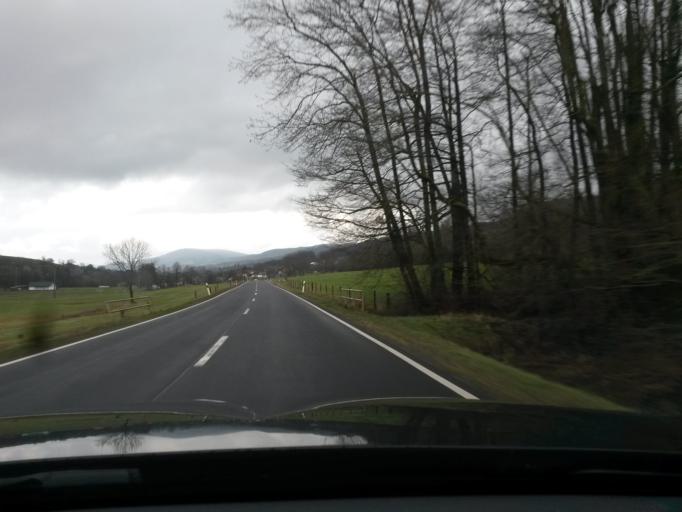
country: DE
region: Thuringia
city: Birx
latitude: 50.5340
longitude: 10.0159
